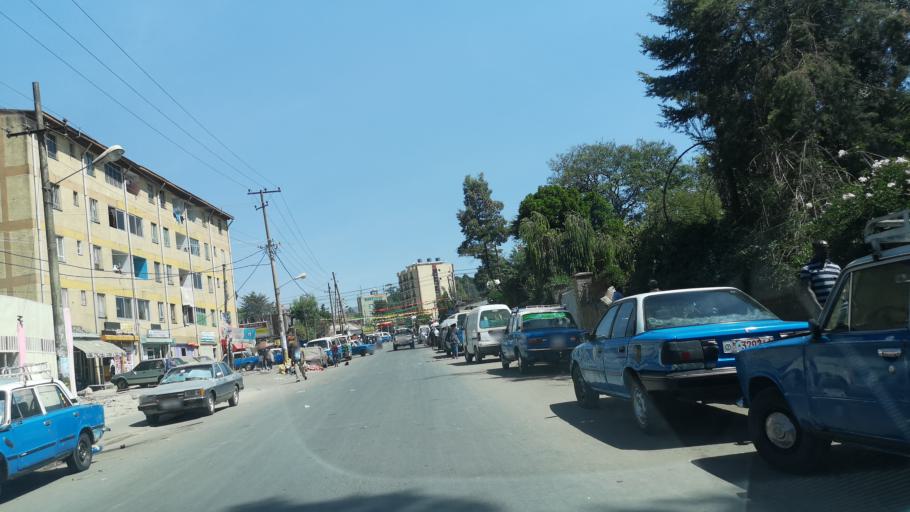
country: ET
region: Adis Abeba
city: Addis Ababa
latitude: 9.0515
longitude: 38.7492
